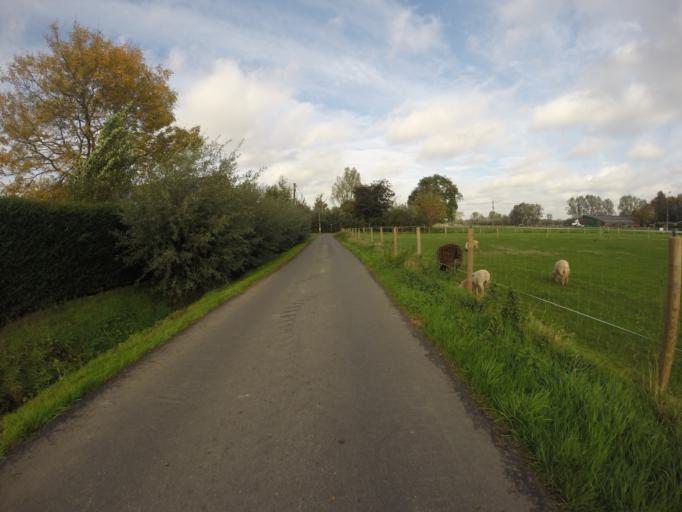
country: BE
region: Flanders
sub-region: Provincie Oost-Vlaanderen
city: Knesselare
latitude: 51.1159
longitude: 3.4133
